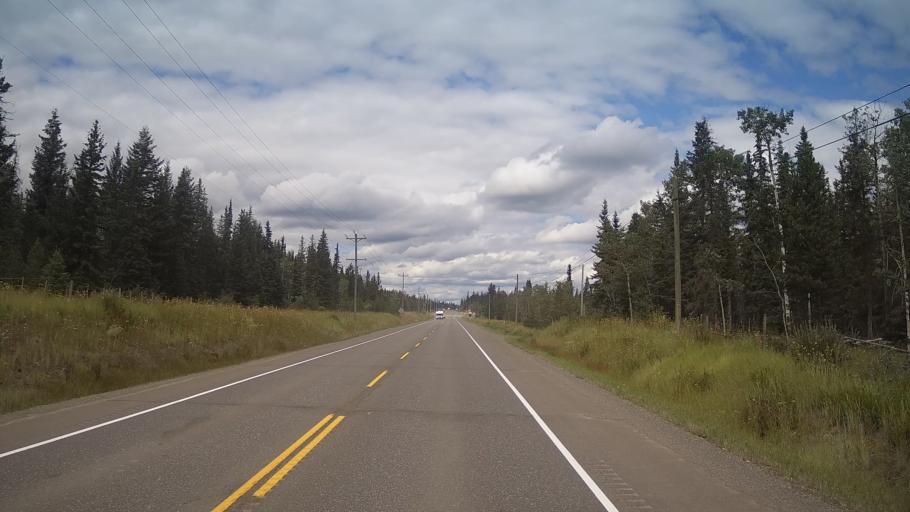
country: CA
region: British Columbia
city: Cache Creek
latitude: 51.1884
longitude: -121.5242
